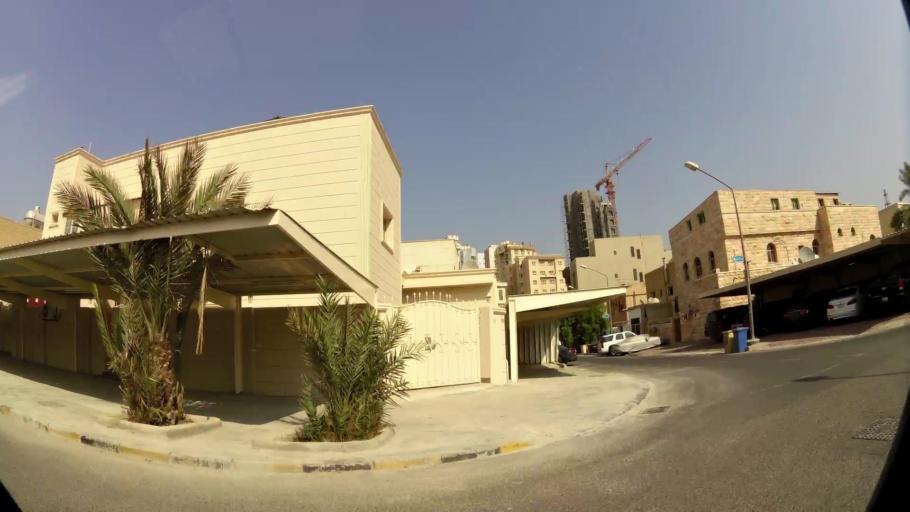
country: KW
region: Muhafazat Hawalli
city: Hawalli
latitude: 29.3465
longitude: 48.0293
